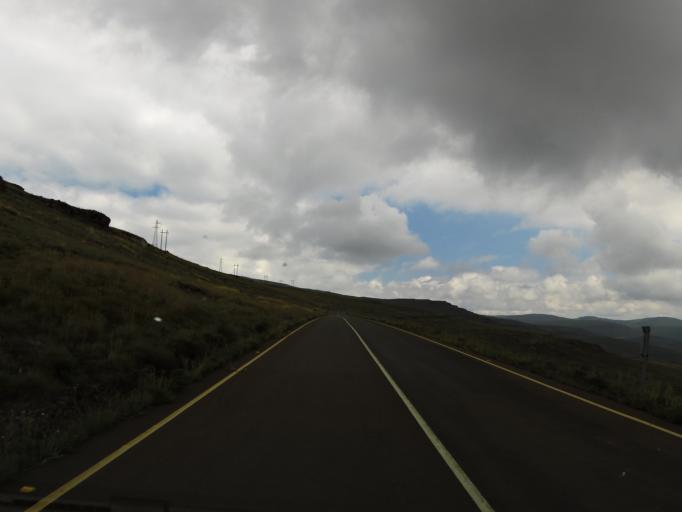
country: LS
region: Butha-Buthe
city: Butha-Buthe
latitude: -29.0914
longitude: 28.4246
